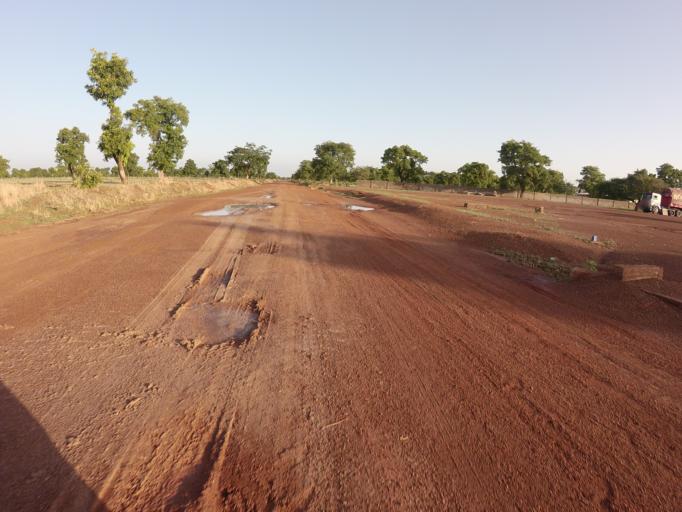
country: TG
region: Savanes
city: Sansanne-Mango
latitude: 10.3002
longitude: -0.0899
